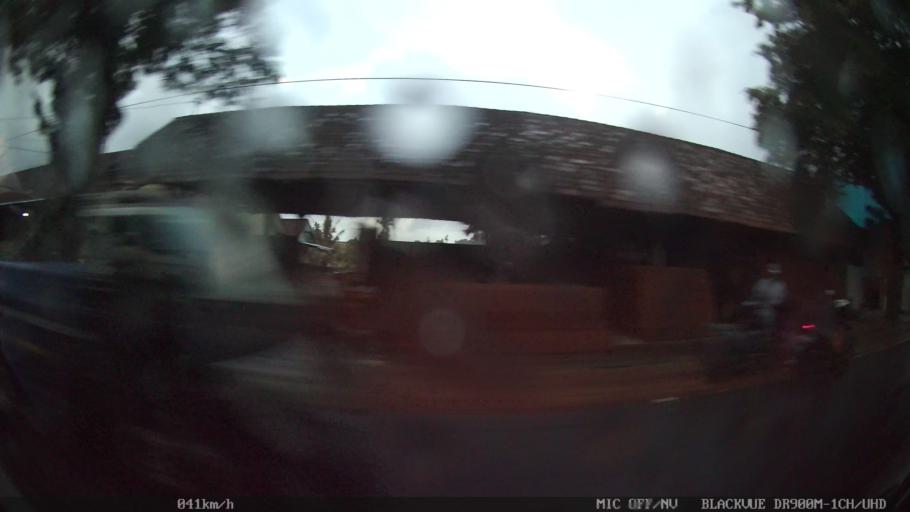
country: ID
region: Bali
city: Banjar Batur
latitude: -8.5925
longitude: 115.2152
